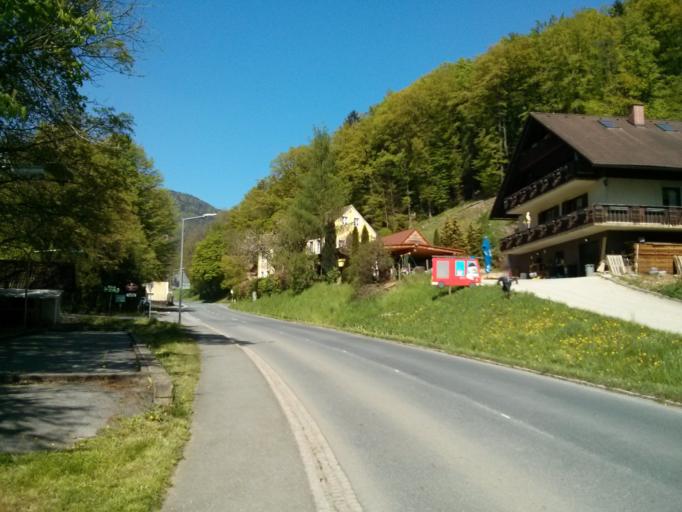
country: AT
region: Styria
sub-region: Politischer Bezirk Graz-Umgebung
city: Stattegg
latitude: 47.1444
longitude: 15.4190
